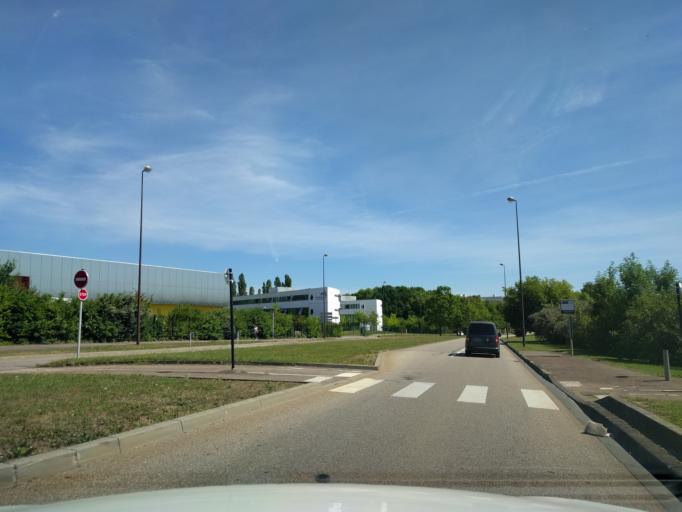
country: FR
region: Lorraine
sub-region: Departement de la Moselle
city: Saint-Julien-les-Metz
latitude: 49.1047
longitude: 6.2148
